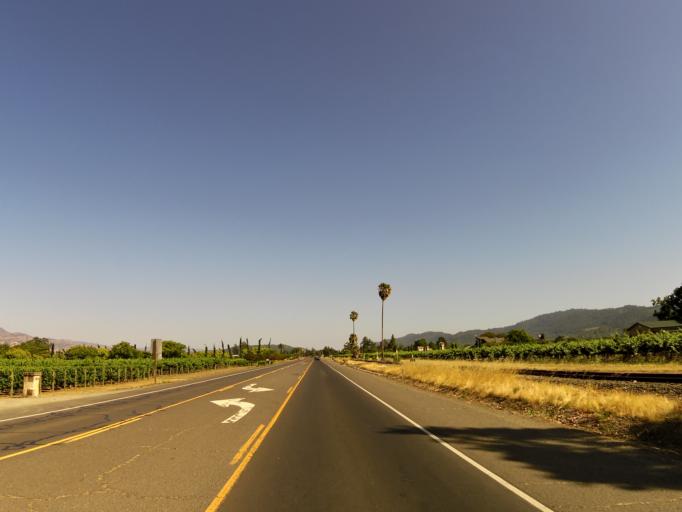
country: US
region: California
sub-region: Napa County
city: Saint Helena
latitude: 38.4565
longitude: -122.4207
